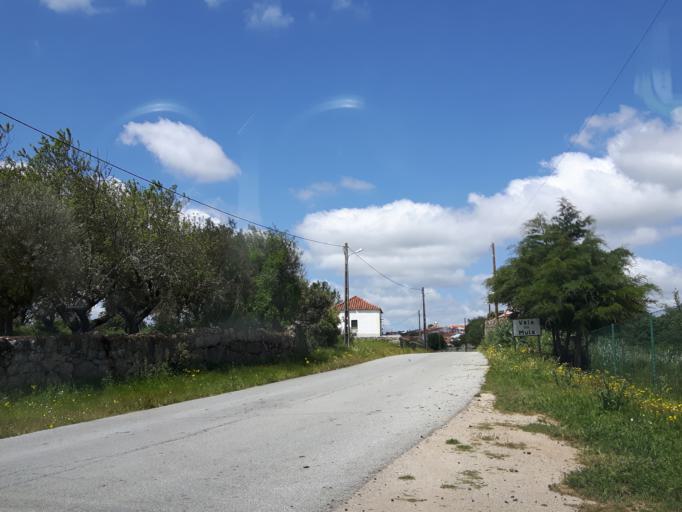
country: ES
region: Castille and Leon
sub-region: Provincia de Salamanca
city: Aldea del Obispo
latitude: 40.7028
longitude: -6.8124
